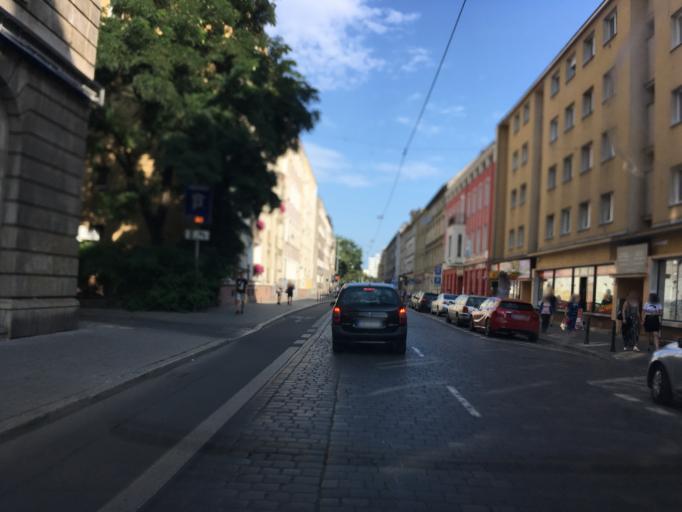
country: PL
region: Lower Silesian Voivodeship
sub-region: Powiat wroclawski
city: Wroclaw
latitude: 51.1027
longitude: 17.0314
